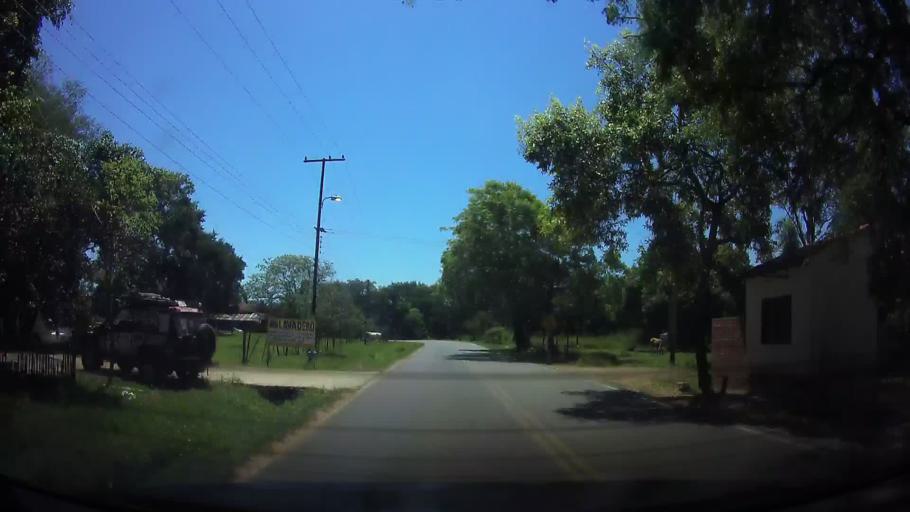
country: PY
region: Central
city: Aregua
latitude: -25.2631
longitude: -57.4214
